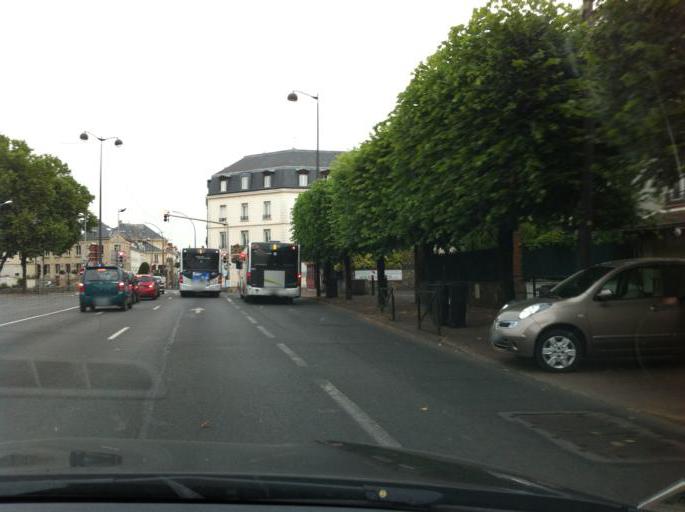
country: FR
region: Ile-de-France
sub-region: Departement de Seine-et-Marne
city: Melun
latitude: 48.5321
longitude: 2.6560
